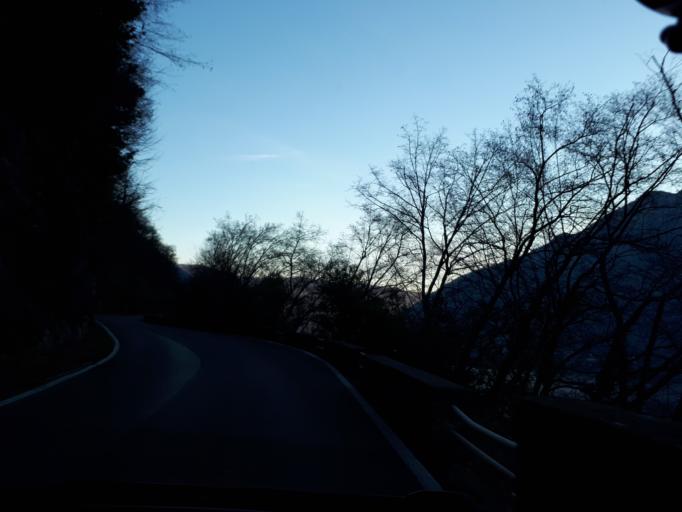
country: IT
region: Lombardy
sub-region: Provincia di Como
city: Nesso
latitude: 45.9250
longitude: 9.1512
